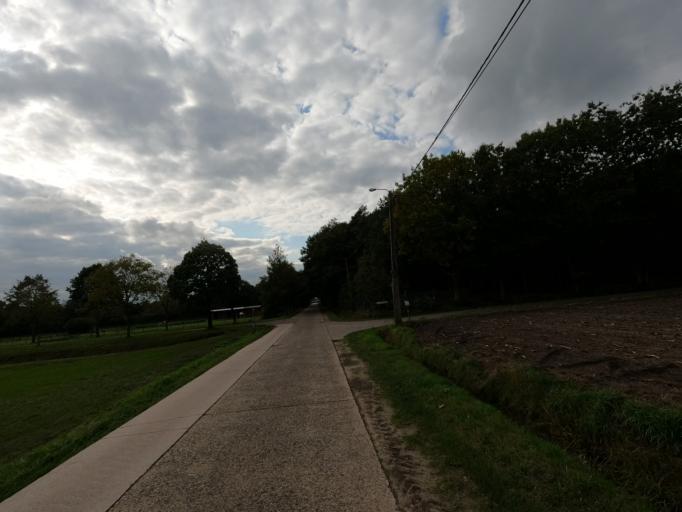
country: BE
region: Flanders
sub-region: Provincie Antwerpen
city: Kasterlee
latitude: 51.2245
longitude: 4.9703
